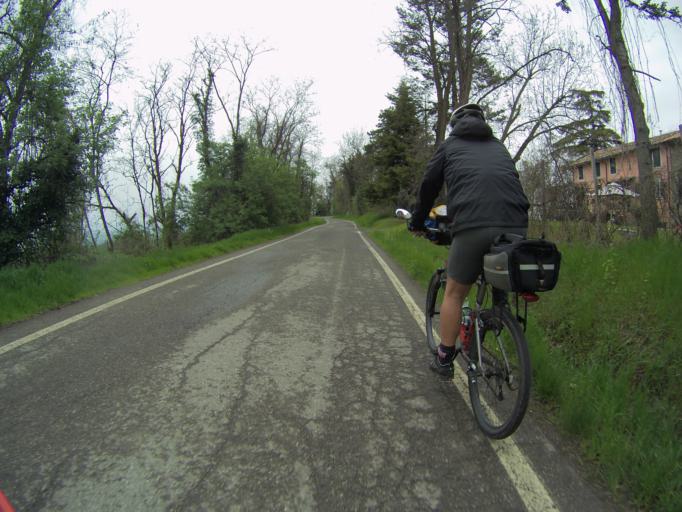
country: IT
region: Emilia-Romagna
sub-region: Provincia di Reggio Emilia
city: Quattro Castella
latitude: 44.6180
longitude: 10.4664
